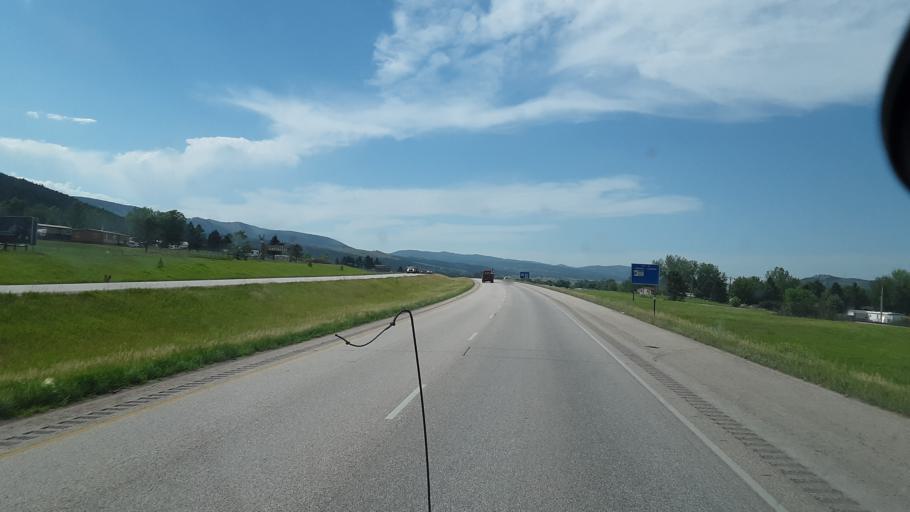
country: US
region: South Dakota
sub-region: Meade County
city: Summerset
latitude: 44.2171
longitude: -103.3673
